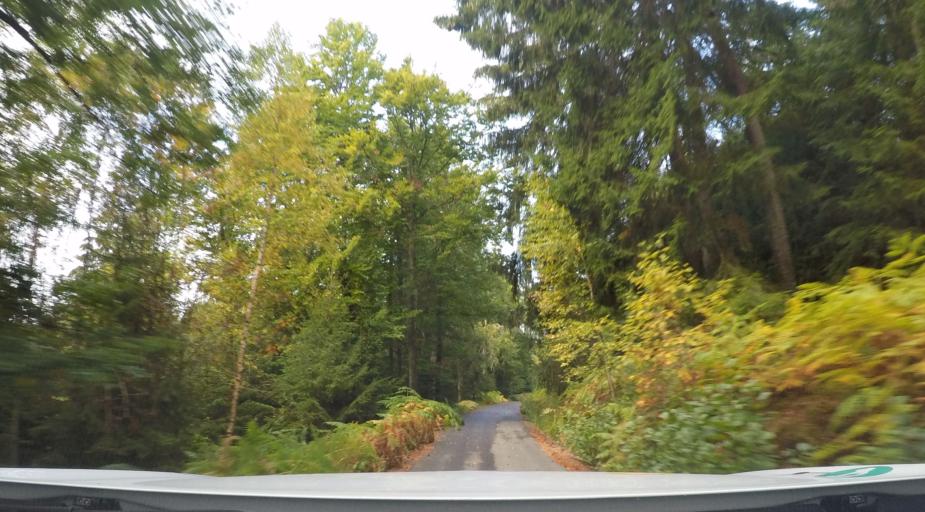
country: DE
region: Baden-Wuerttemberg
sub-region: Karlsruhe Region
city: Biberach
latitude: 48.5655
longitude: 8.3277
